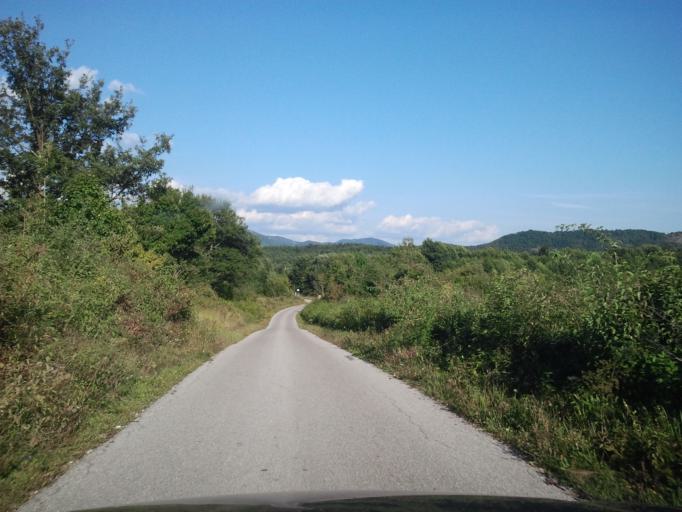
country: HR
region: Zadarska
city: Obrovac
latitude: 44.3527
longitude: 15.6740
